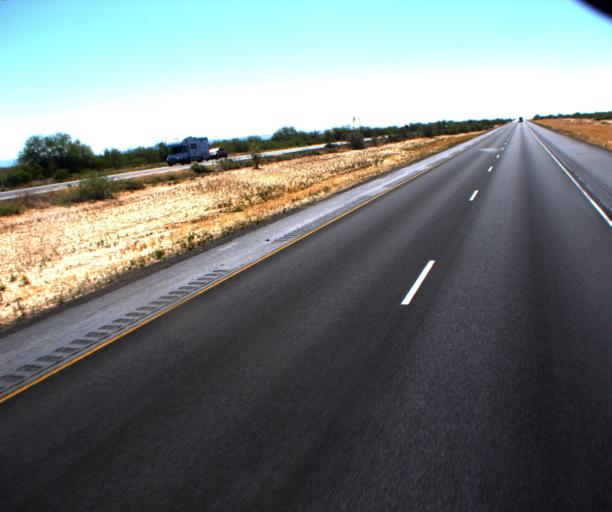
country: US
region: Arizona
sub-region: Yavapai County
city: Congress
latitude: 34.0962
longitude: -112.9121
